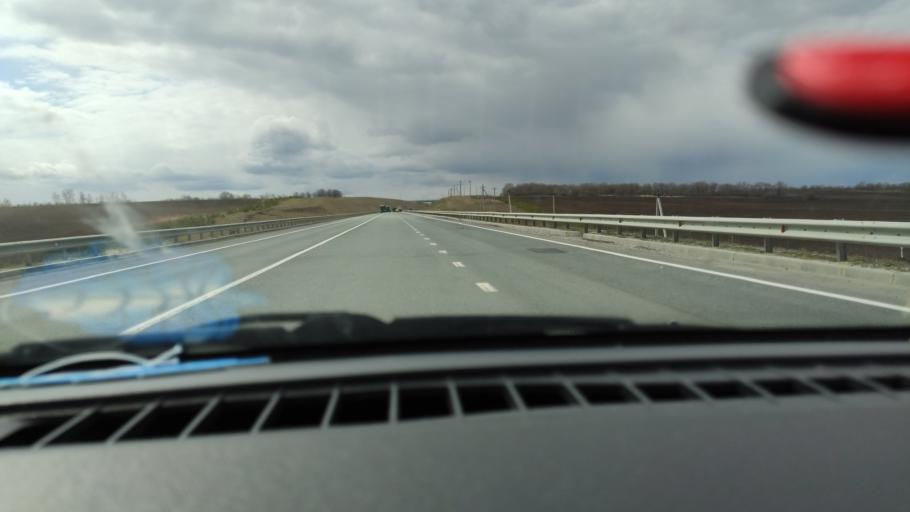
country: RU
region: Saratov
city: Yelshanka
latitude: 51.8204
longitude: 46.3663
